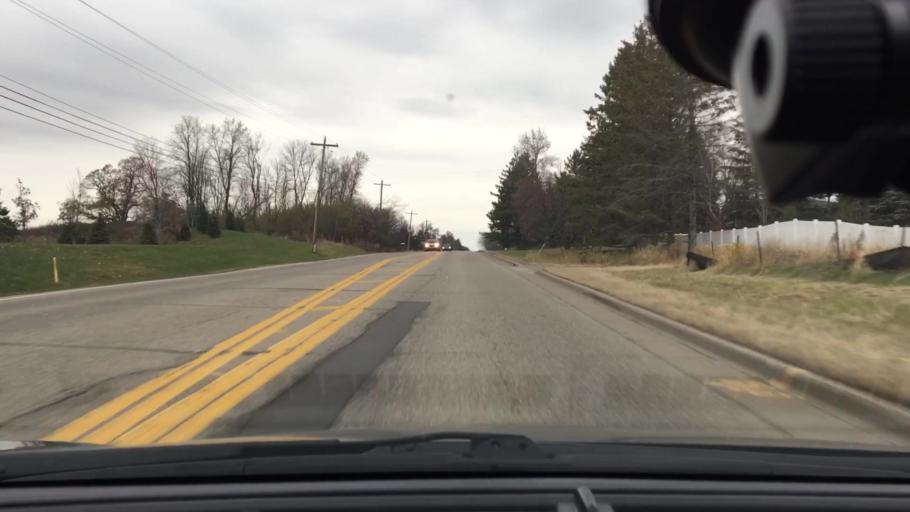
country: US
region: Minnesota
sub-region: Hennepin County
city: Corcoran
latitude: 45.0702
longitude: -93.5220
